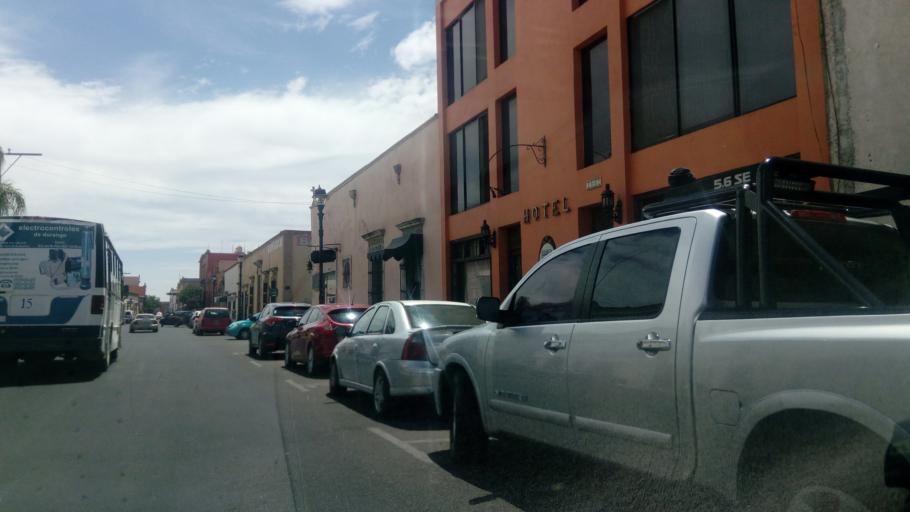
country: MX
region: Durango
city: Victoria de Durango
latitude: 24.0253
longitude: -104.6737
